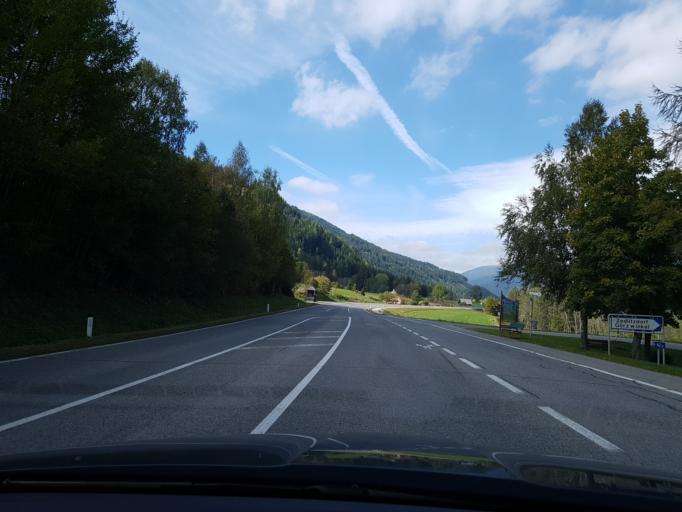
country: AT
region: Carinthia
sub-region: Politischer Bezirk Feldkirchen
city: Gnesau
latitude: 46.7941
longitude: 13.9187
